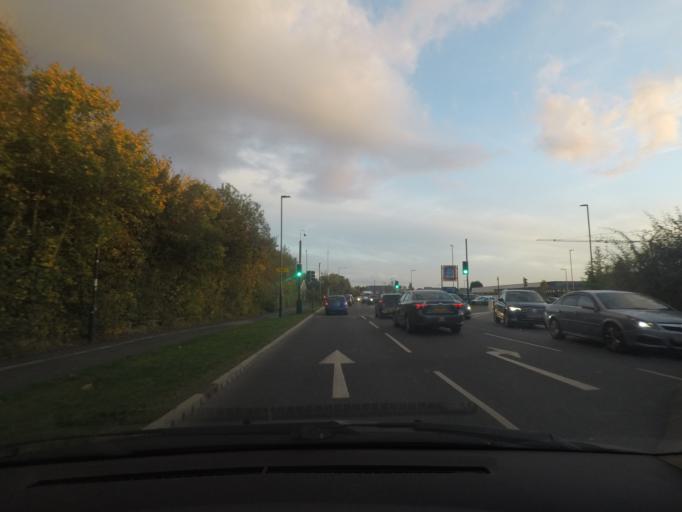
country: GB
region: England
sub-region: City of York
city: York
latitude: 53.9849
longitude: -1.0951
